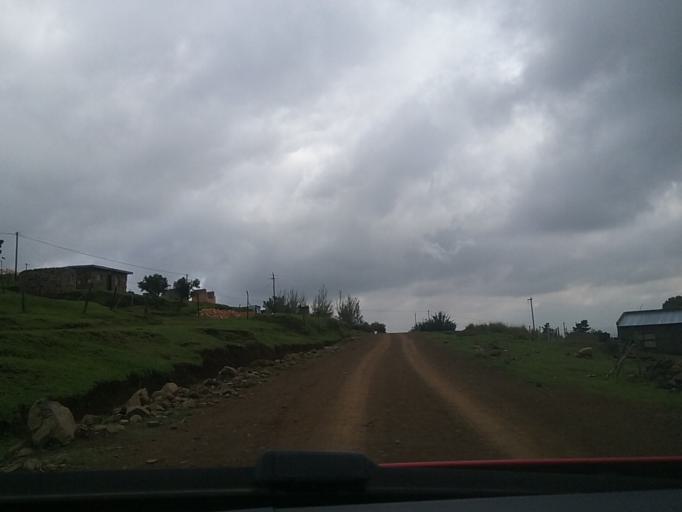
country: LS
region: Berea
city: Teyateyaneng
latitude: -29.2469
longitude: 27.8416
